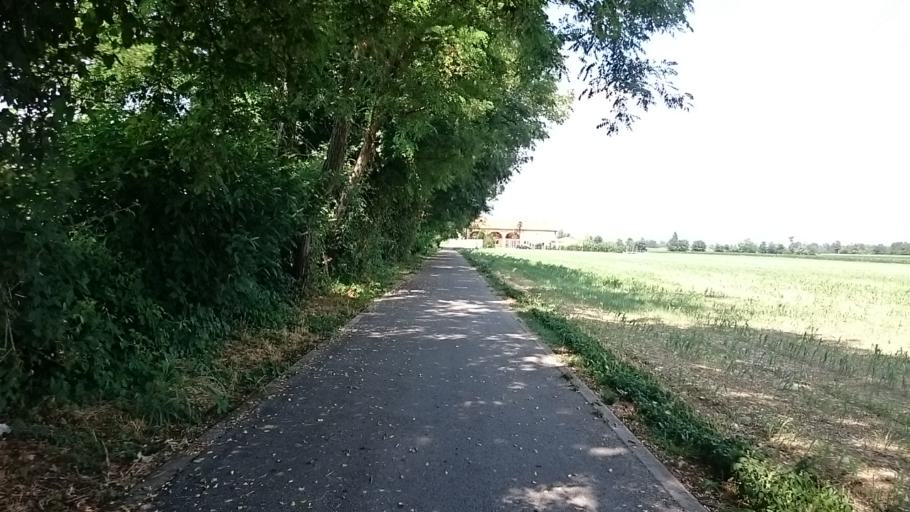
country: IT
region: Veneto
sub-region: Provincia di Vicenza
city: Rosa
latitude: 45.7099
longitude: 11.7374
